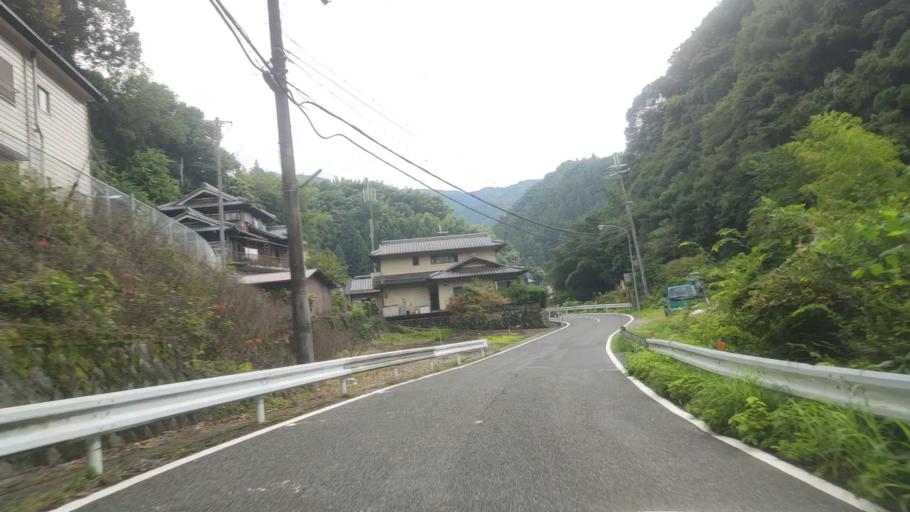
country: JP
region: Wakayama
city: Hashimoto
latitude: 34.2648
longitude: 135.5507
